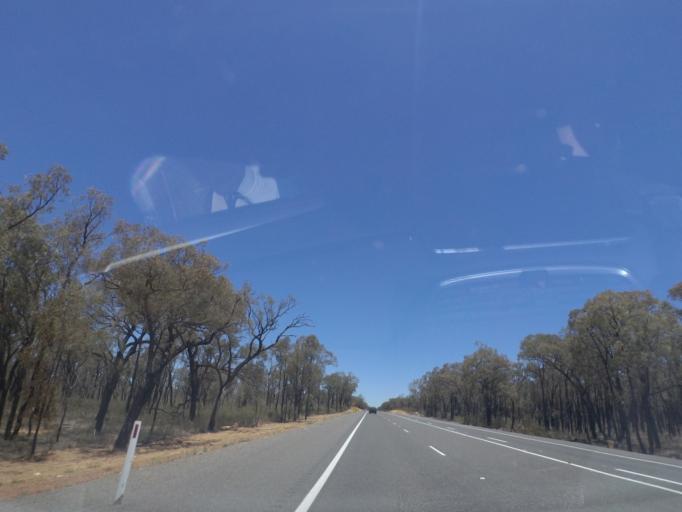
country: AU
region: New South Wales
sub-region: Warrumbungle Shire
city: Coonabarabran
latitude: -30.8994
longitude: 149.4398
